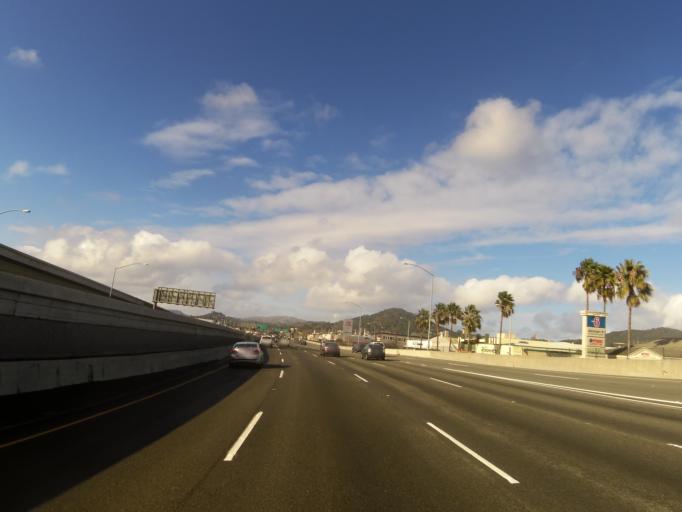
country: US
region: California
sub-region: Marin County
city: San Rafael
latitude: 37.9629
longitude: -122.5109
